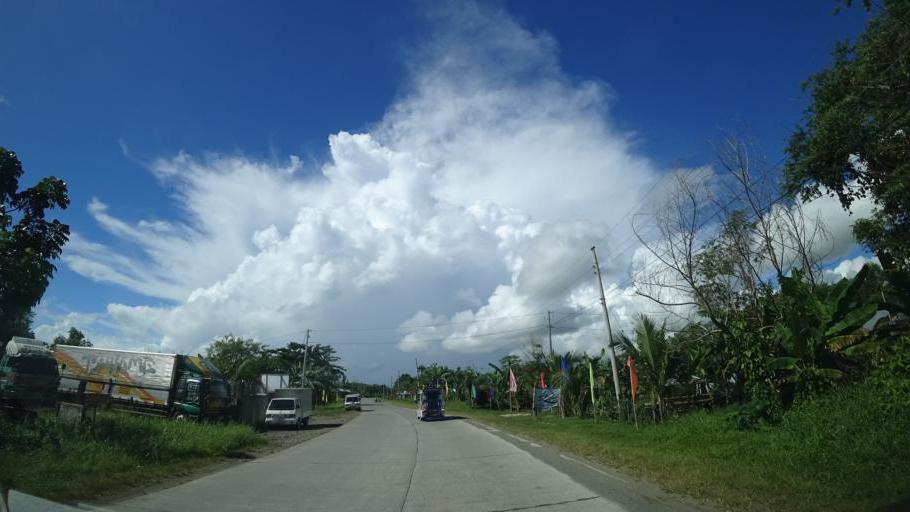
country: PH
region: Eastern Visayas
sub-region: Province of Leyte
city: Palo
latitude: 11.1571
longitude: 125.0014
